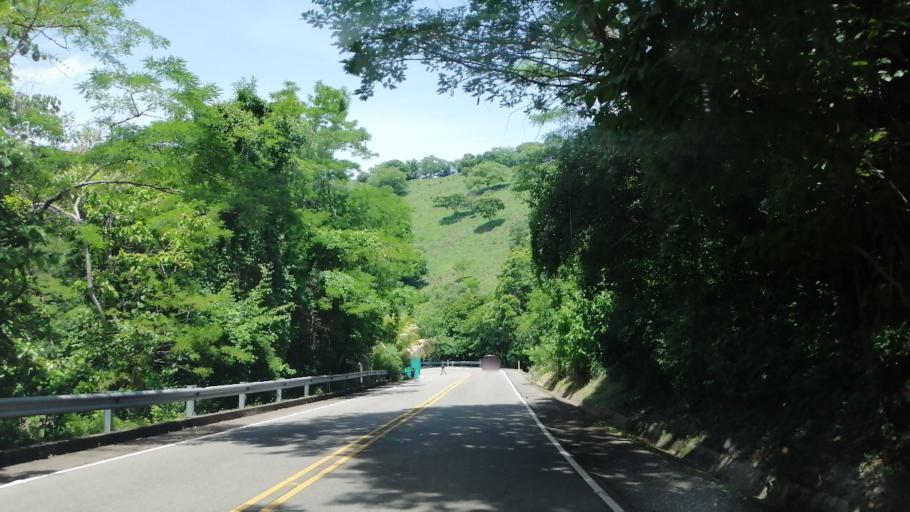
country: SV
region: Chalatenango
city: Nueva Concepcion
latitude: 14.1706
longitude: -89.3110
